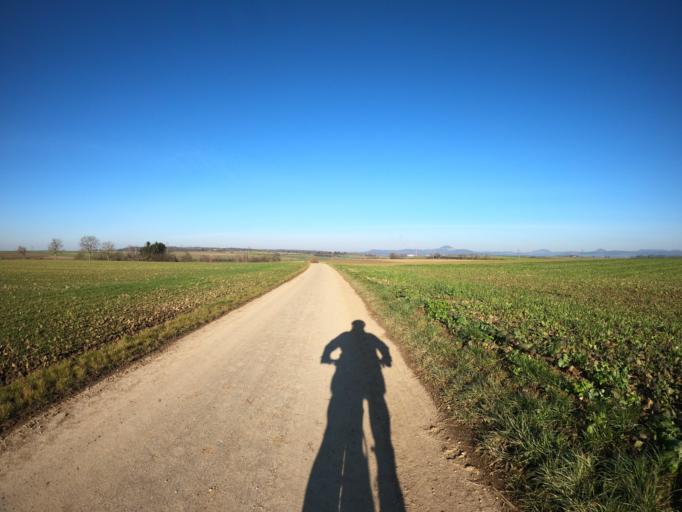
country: DE
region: Baden-Wuerttemberg
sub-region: Regierungsbezirk Stuttgart
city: Heiningen
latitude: 48.6655
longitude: 9.6629
